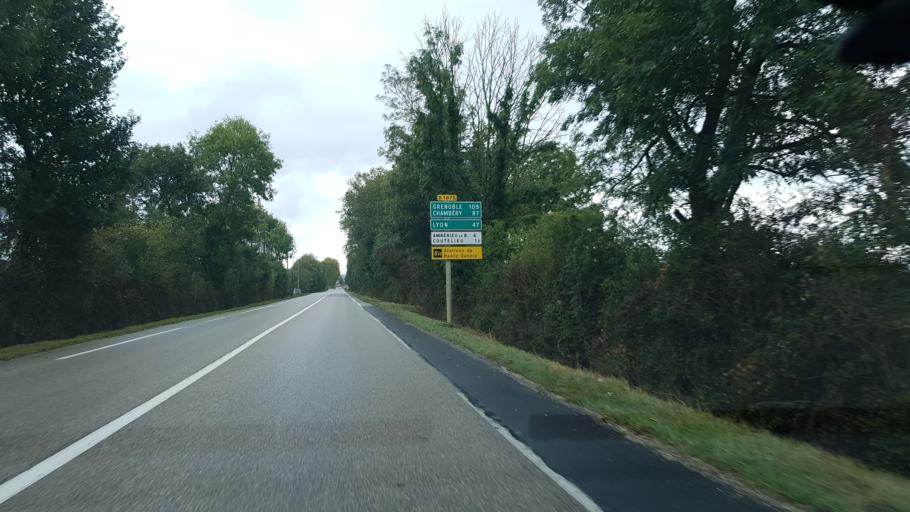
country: FR
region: Rhone-Alpes
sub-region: Departement de l'Ain
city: Ambronay
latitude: 46.0081
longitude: 5.3411
